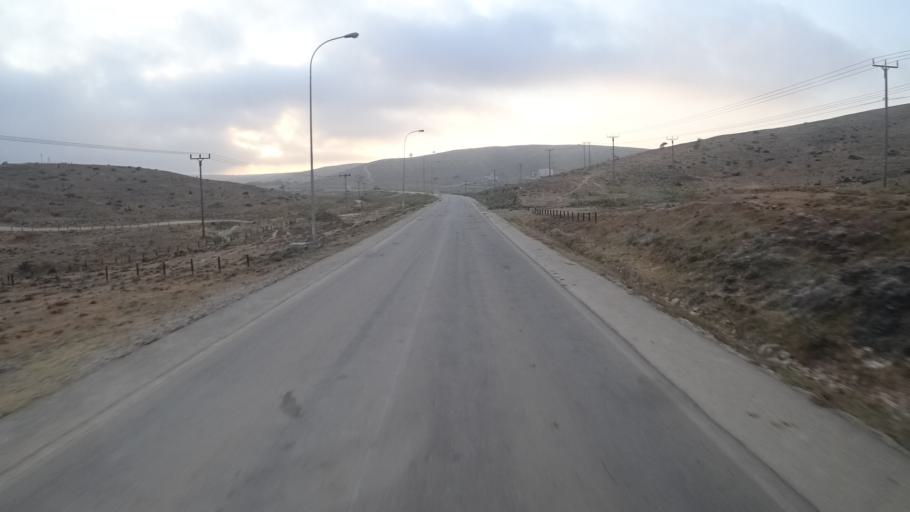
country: OM
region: Zufar
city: Salalah
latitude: 17.1267
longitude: 53.9477
